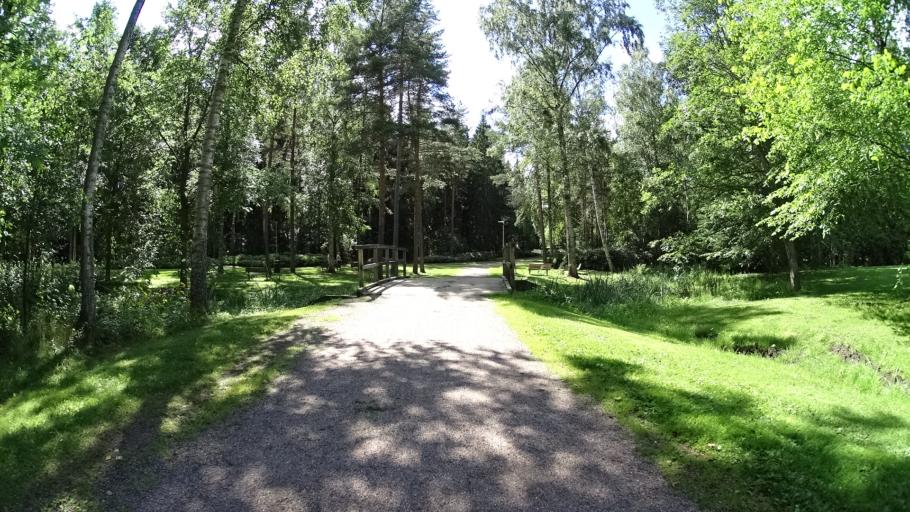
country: FI
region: Uusimaa
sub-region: Helsinki
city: Teekkarikylae
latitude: 60.2851
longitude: 24.8571
